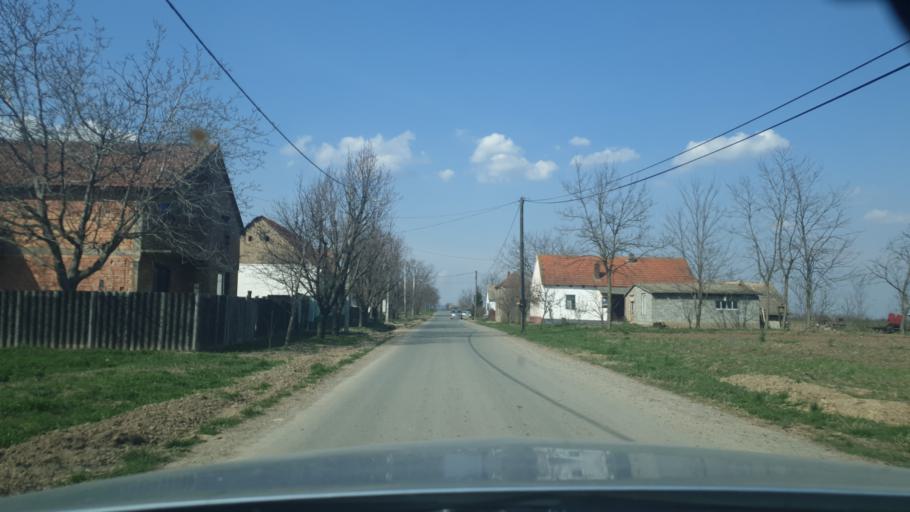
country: RS
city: Putinci
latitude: 45.0421
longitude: 19.9397
